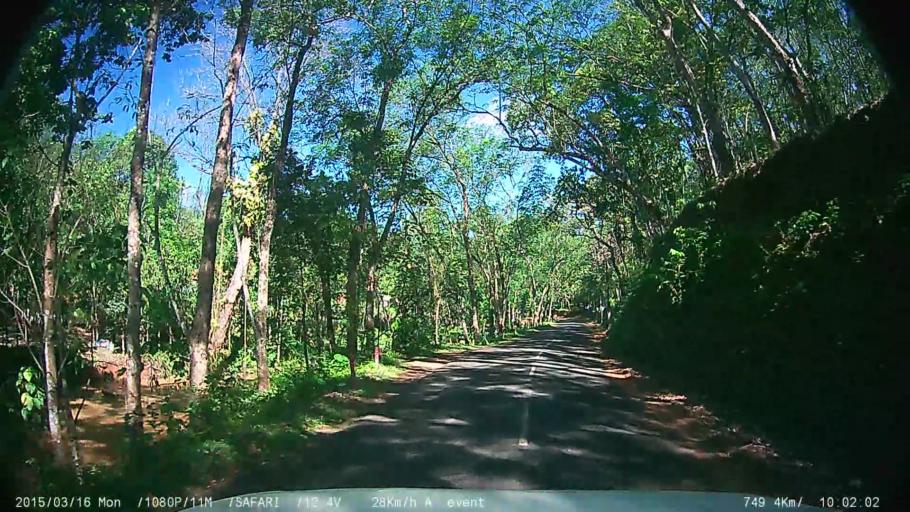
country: IN
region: Kerala
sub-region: Kottayam
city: Palackattumala
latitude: 9.7821
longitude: 76.5807
